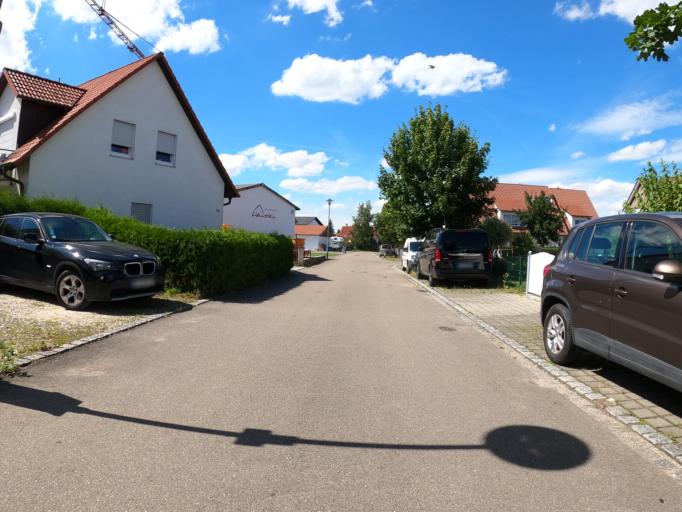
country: DE
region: Bavaria
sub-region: Swabia
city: Leipheim
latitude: 48.4164
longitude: 10.1948
